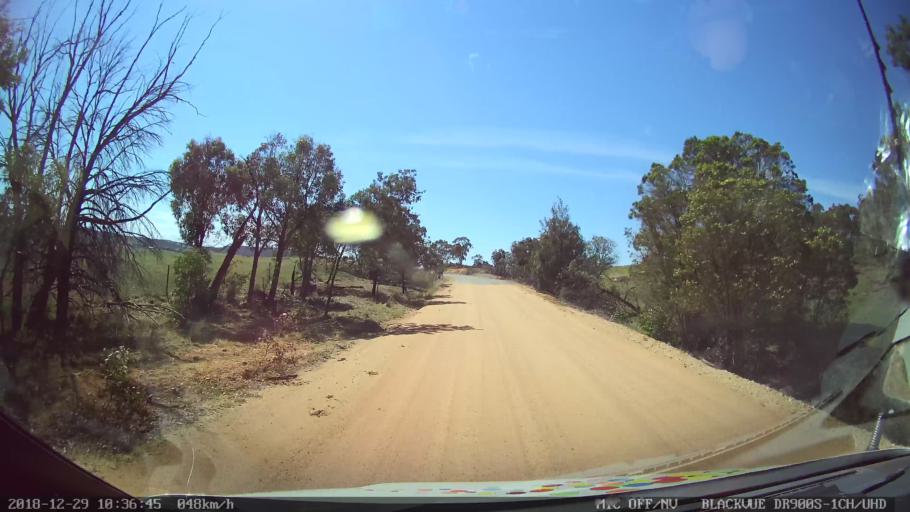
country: AU
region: New South Wales
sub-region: Yass Valley
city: Gundaroo
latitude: -34.9954
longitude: 149.4928
